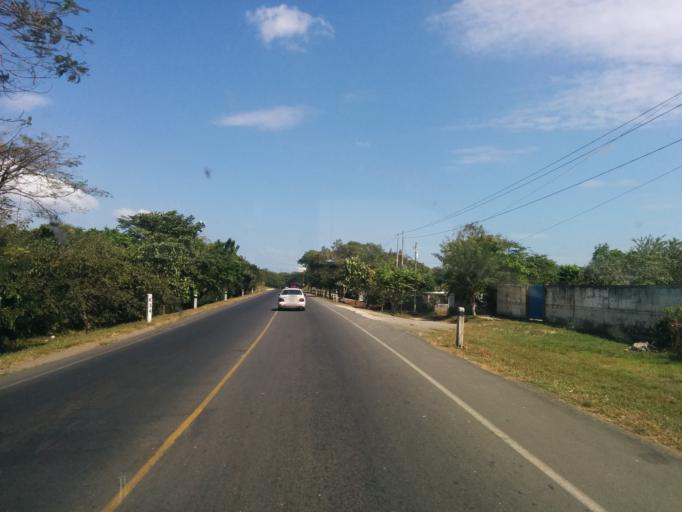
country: NI
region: Masaya
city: Masaya
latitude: 11.9592
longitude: -86.0868
